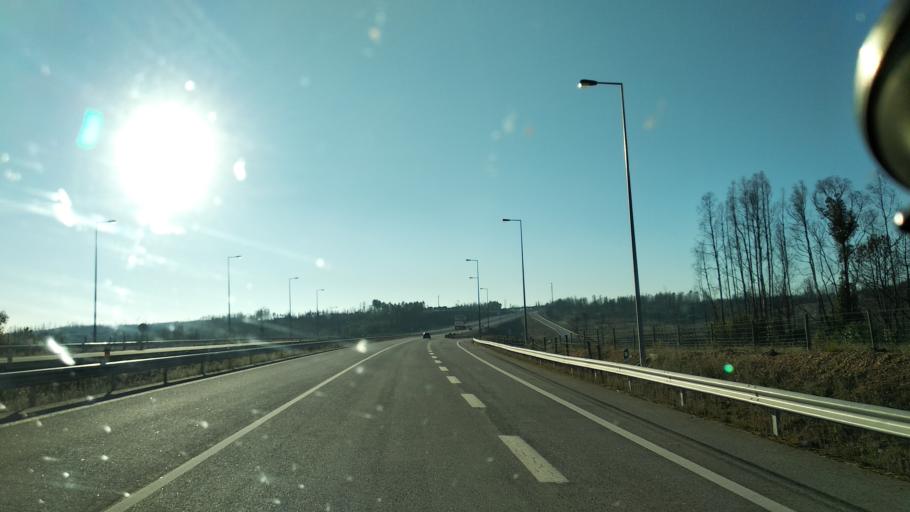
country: PT
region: Santarem
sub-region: Macao
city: Macao
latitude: 39.5319
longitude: -7.9424
